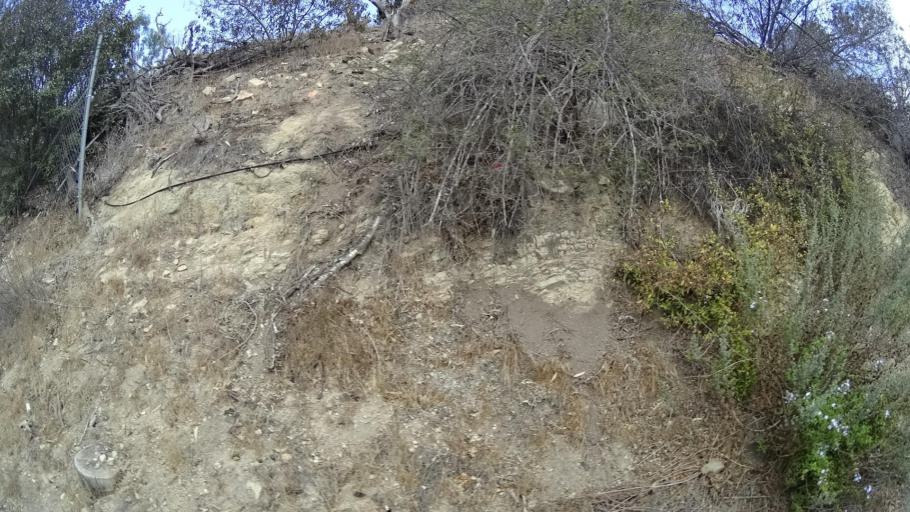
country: US
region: California
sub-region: San Diego County
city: Fallbrook
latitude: 33.4251
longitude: -117.3040
